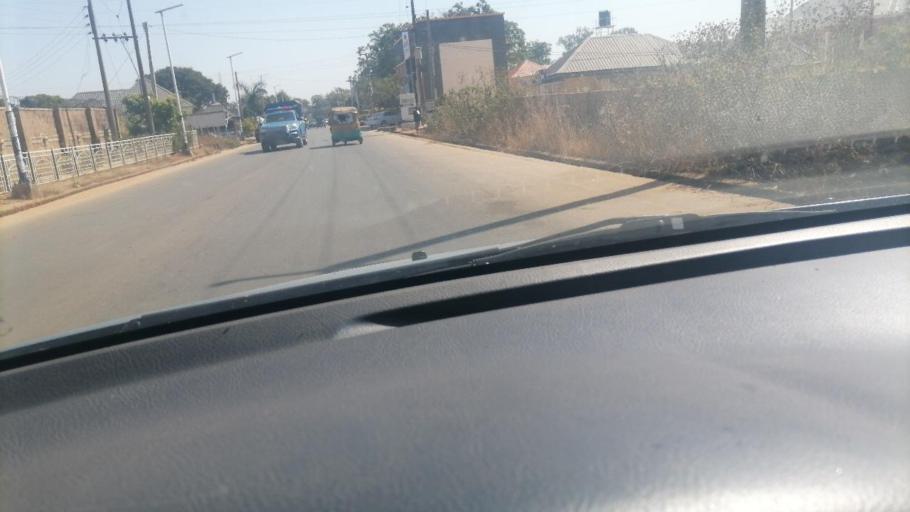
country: NG
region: Plateau
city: Jos
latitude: 9.8652
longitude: 8.9034
